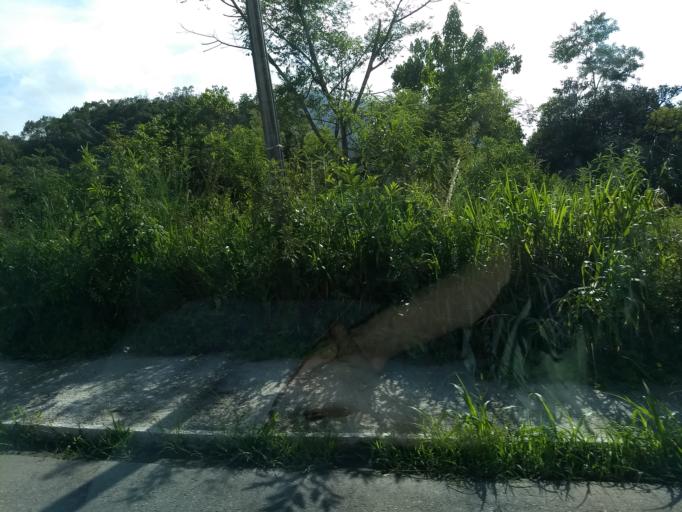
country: BR
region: Santa Catarina
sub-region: Jaragua Do Sul
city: Jaragua do Sul
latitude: -26.4607
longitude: -49.1049
